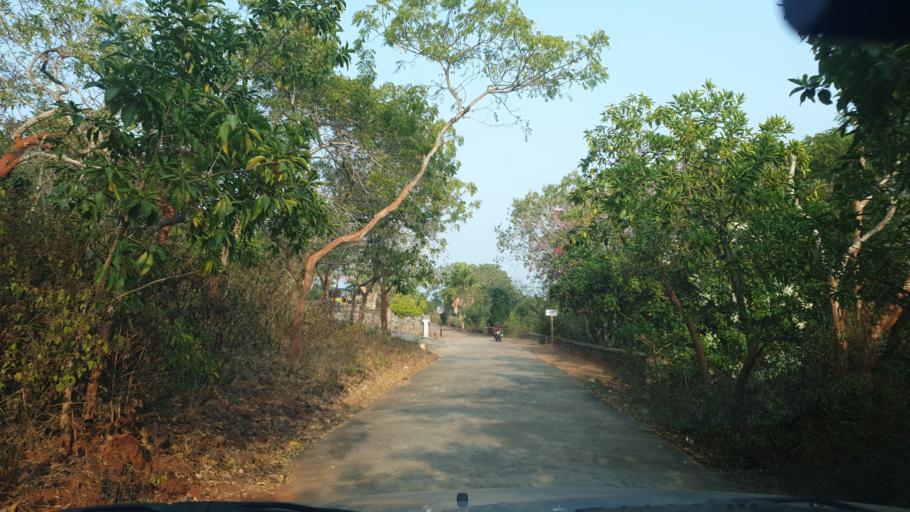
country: IN
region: Andhra Pradesh
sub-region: Srikakulam
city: Narasannapeta
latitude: 18.3329
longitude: 84.0456
